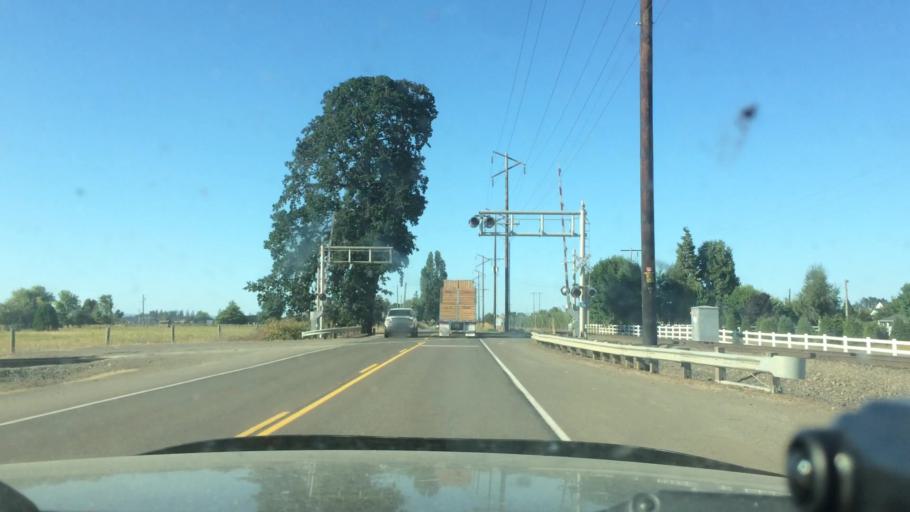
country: US
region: Oregon
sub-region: Marion County
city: Hayesville
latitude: 45.0555
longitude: -122.9846
